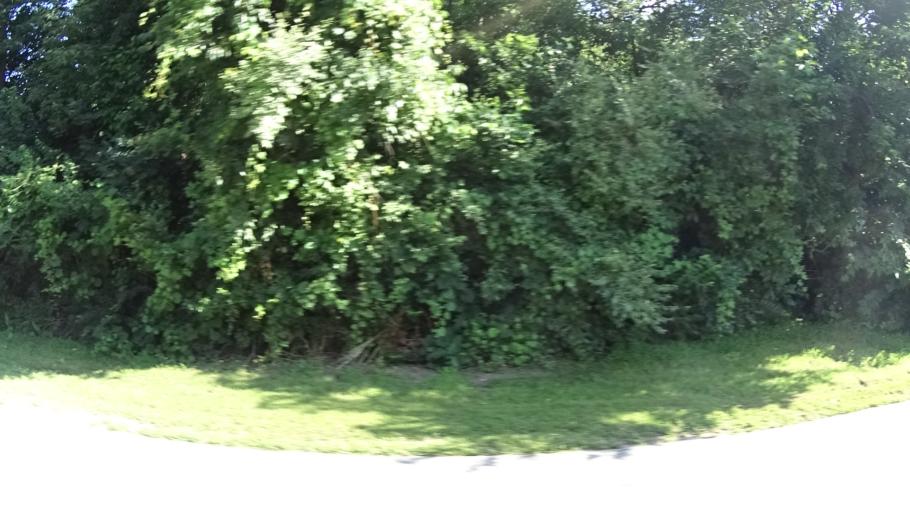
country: US
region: Ohio
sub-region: Huron County
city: Bellevue
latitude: 41.3721
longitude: -82.8375
